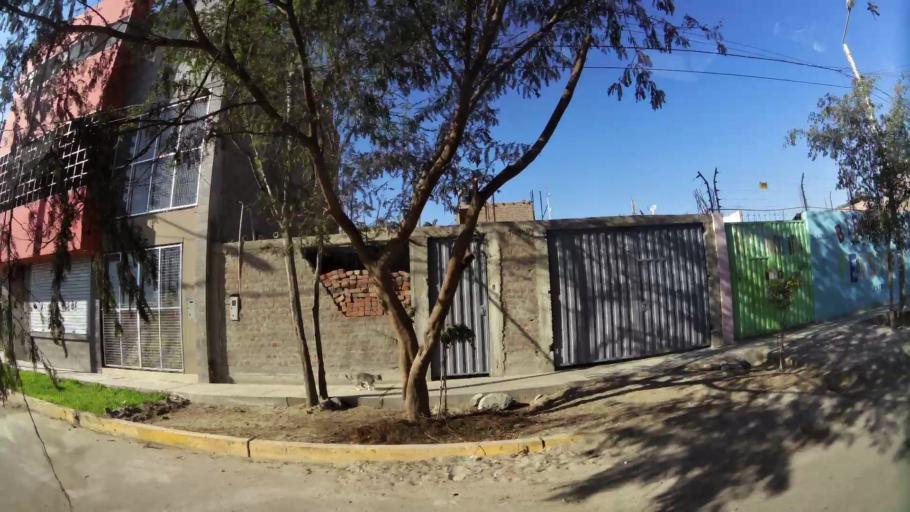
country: PE
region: Ica
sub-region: Provincia de Ica
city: La Tinguina
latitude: -14.0455
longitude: -75.7011
